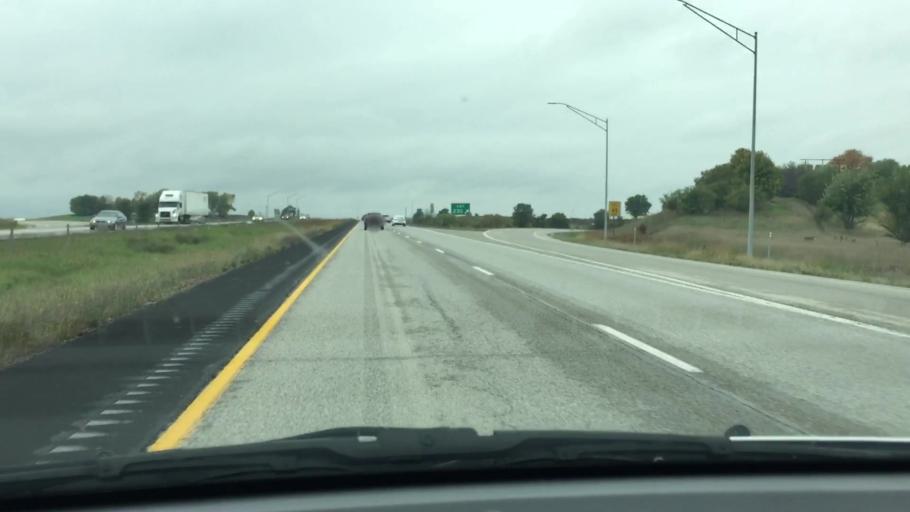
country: US
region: Iowa
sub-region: Johnson County
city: Tiffin
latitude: 41.6878
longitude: -91.7983
